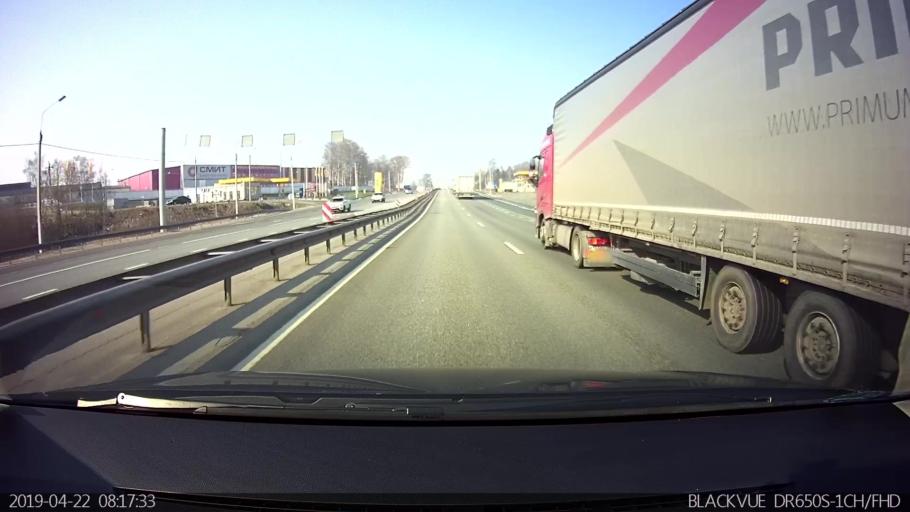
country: RU
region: Smolensk
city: Yartsevo
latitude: 55.0775
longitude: 32.6695
